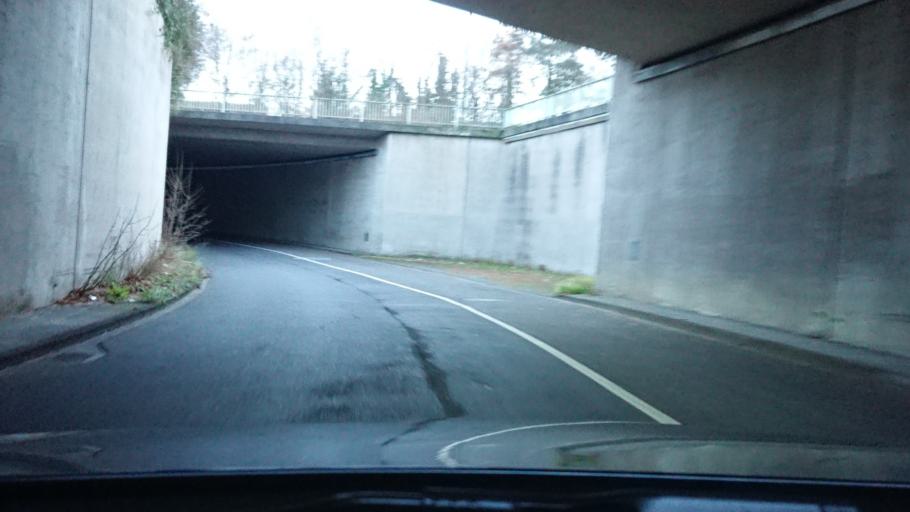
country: DE
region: North Rhine-Westphalia
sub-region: Regierungsbezirk Koln
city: Bilderstoeckchen
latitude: 51.0005
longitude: 6.9129
